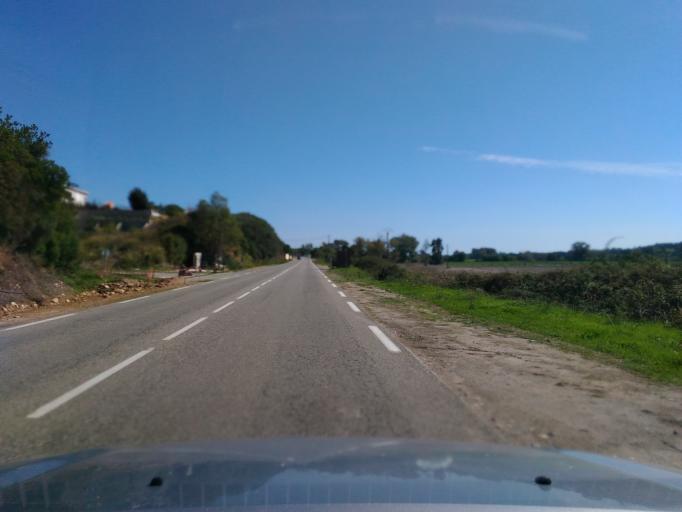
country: FR
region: Corsica
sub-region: Departement de la Haute-Corse
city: Aleria
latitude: 42.1136
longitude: 9.5039
